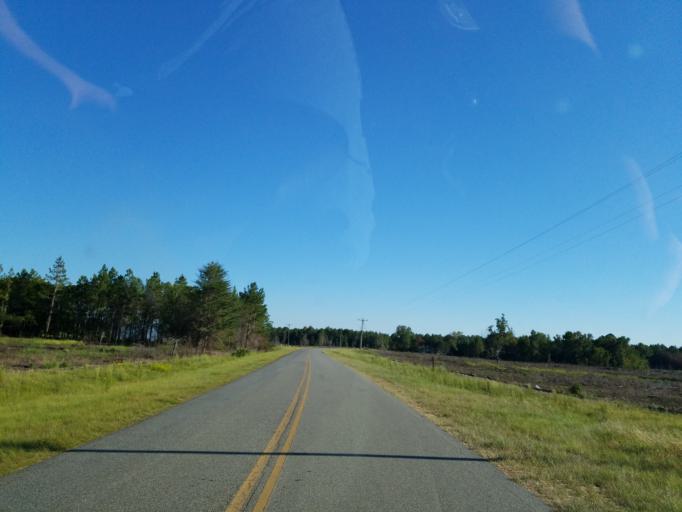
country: US
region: Georgia
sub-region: Dooly County
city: Vienna
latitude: 32.0704
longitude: -83.9557
